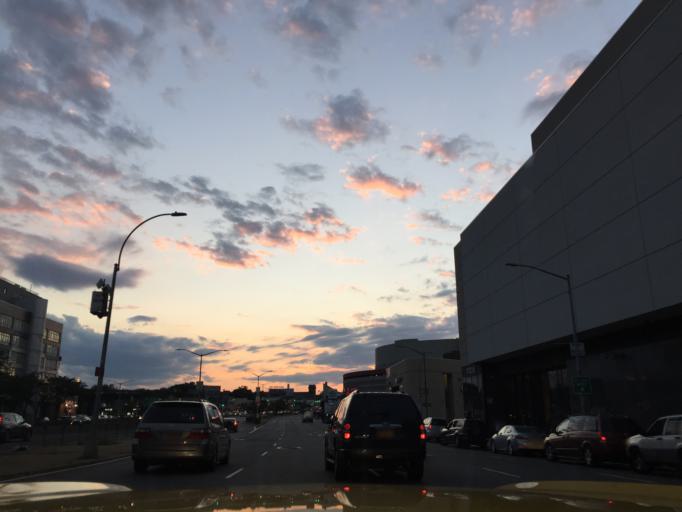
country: US
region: New York
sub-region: Queens County
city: Borough of Queens
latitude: 40.7340
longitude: -73.8713
